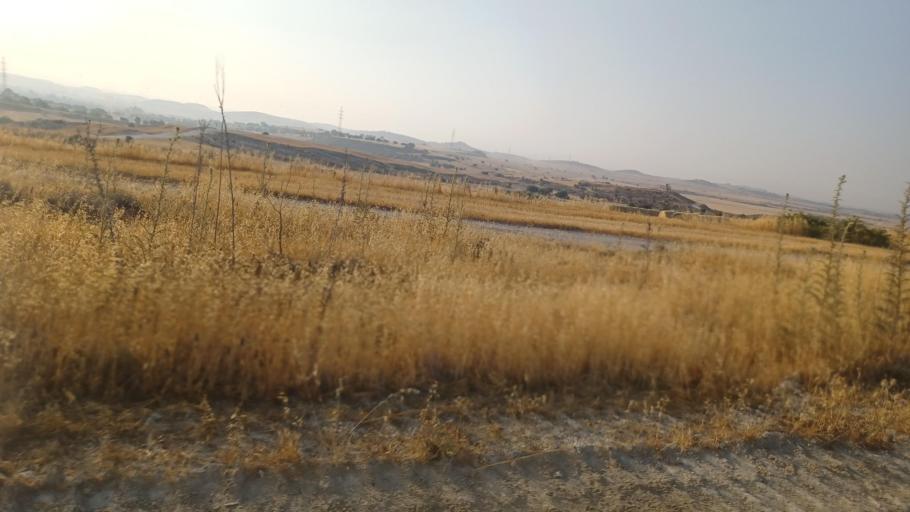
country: CY
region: Larnaka
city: Psevdas
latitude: 34.9234
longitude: 33.5147
